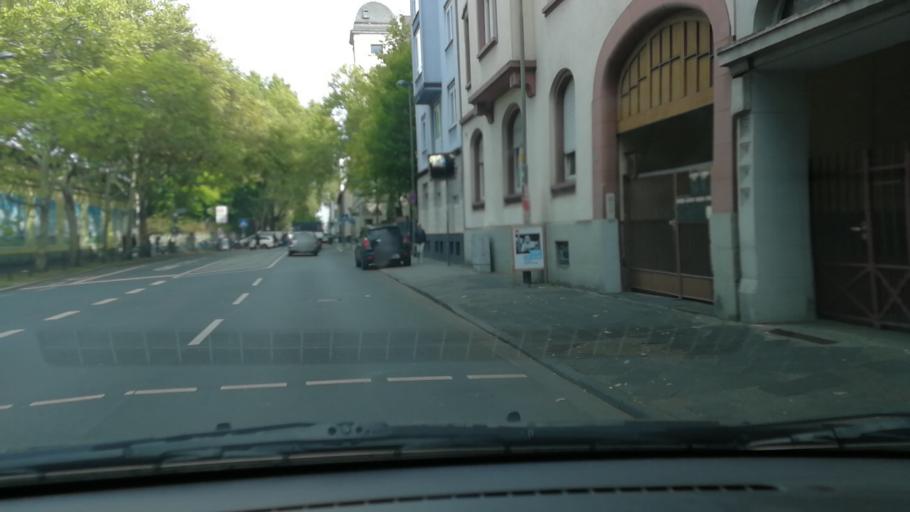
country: DE
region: Hesse
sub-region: Regierungsbezirk Darmstadt
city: Offenbach
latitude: 50.0986
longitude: 8.7600
